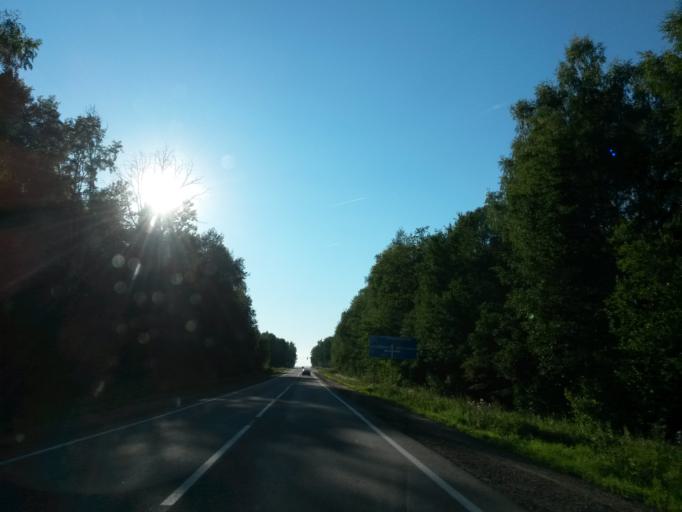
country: RU
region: Jaroslavl
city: Gavrilov-Yam
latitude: 57.2713
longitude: 39.9557
